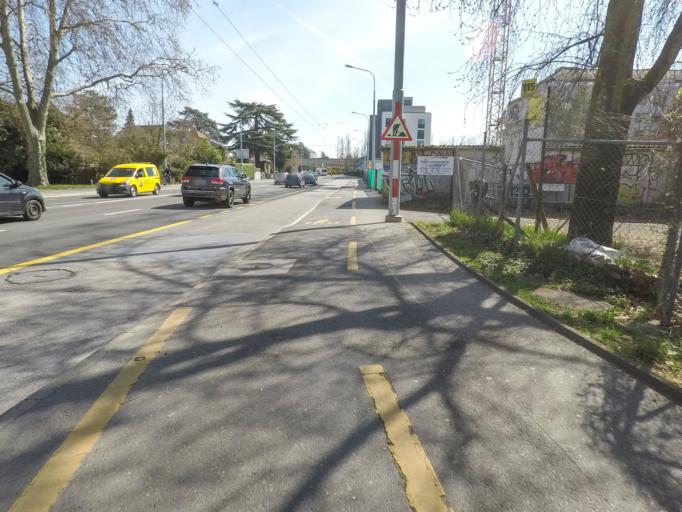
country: CH
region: Geneva
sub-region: Geneva
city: Les Avanchets
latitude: 46.2119
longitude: 6.1061
